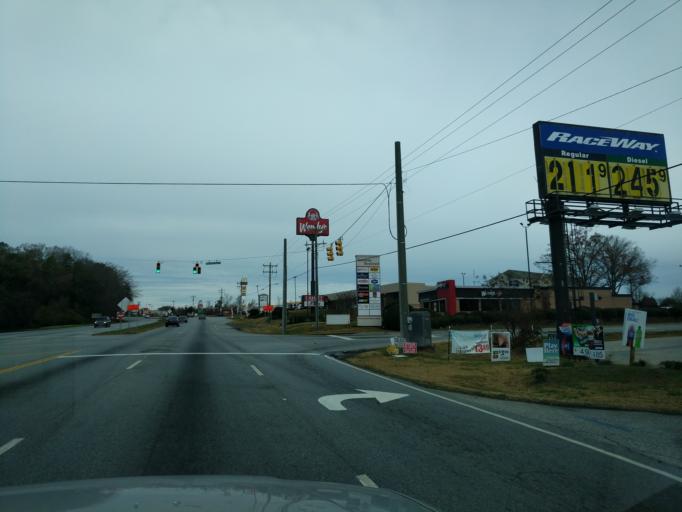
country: US
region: South Carolina
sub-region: Anderson County
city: Northlake
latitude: 34.5758
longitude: -82.7122
